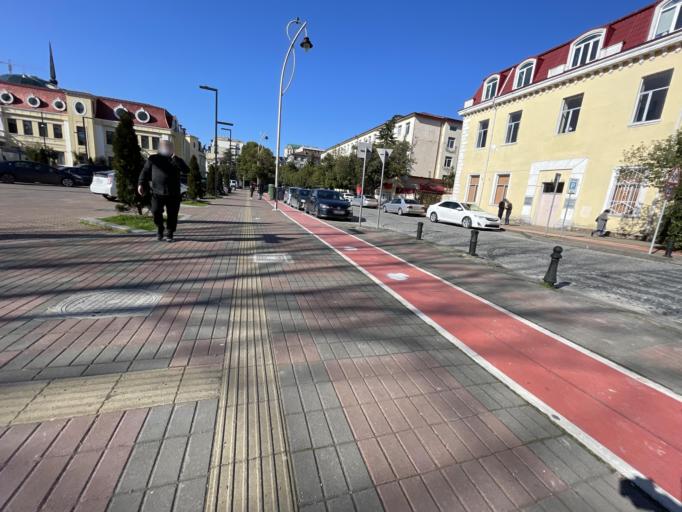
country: GE
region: Ajaria
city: Batumi
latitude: 41.6464
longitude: 41.6379
